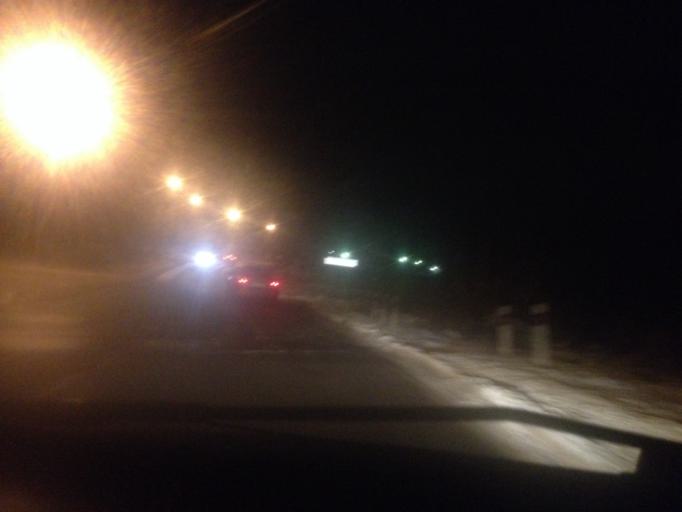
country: RU
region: Tula
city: Barsuki
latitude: 54.2555
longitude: 37.4882
